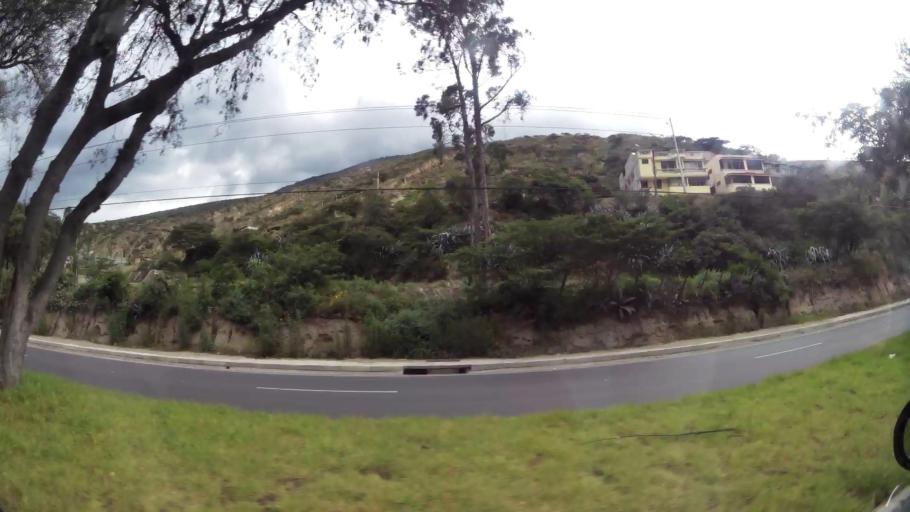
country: EC
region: Pichincha
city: Quito
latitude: -0.0341
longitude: -78.4538
